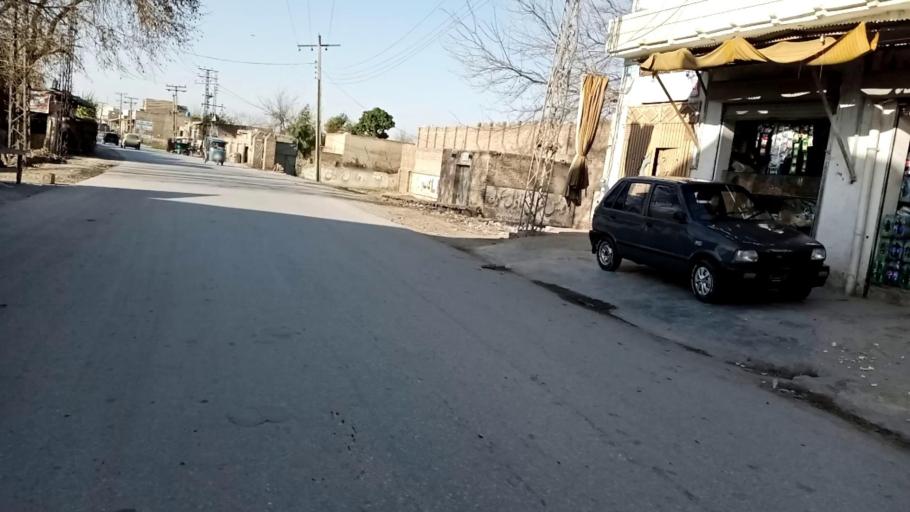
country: PK
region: Khyber Pakhtunkhwa
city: Peshawar
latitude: 34.0764
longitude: 71.5334
